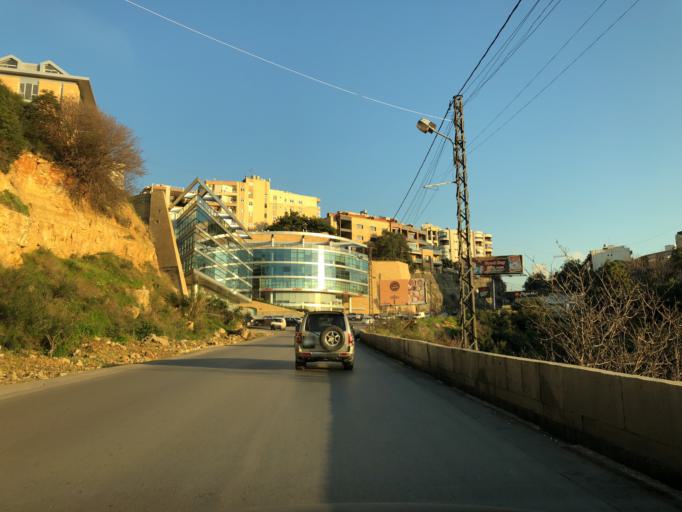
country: LB
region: Mont-Liban
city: Baabda
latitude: 33.8563
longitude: 35.5629
